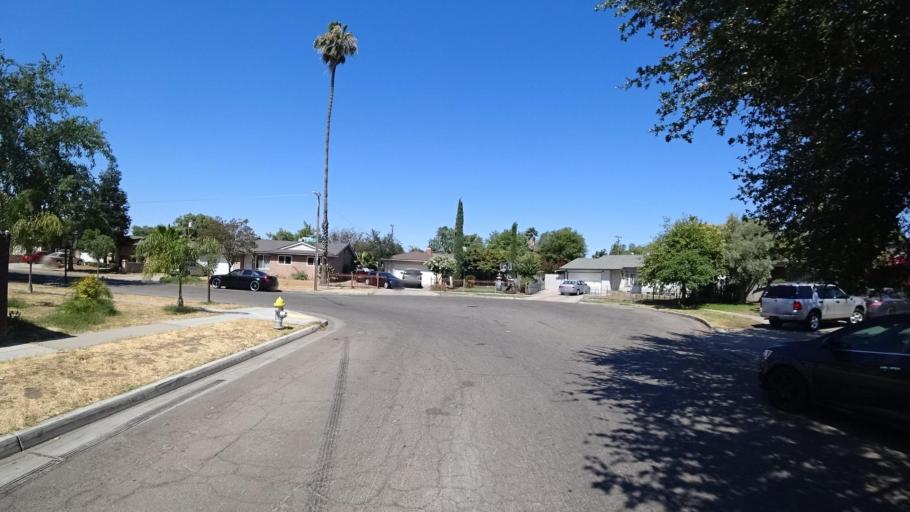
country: US
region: California
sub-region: Fresno County
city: Fresno
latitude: 36.7229
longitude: -119.7396
